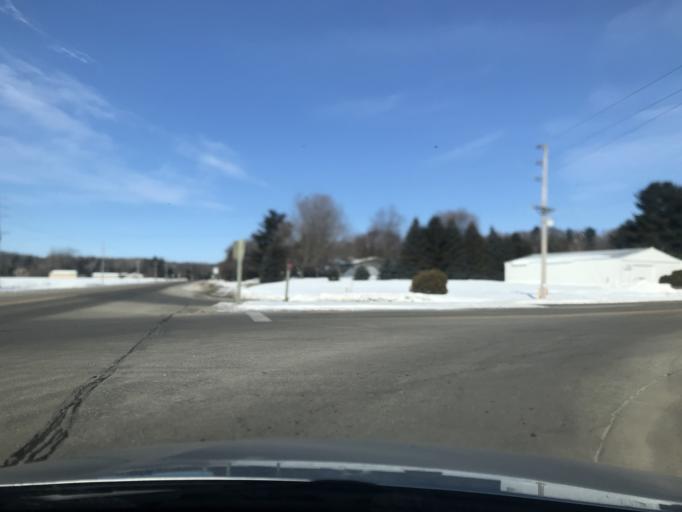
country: US
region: Wisconsin
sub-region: Oconto County
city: Oconto Falls
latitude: 44.8851
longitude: -88.1561
